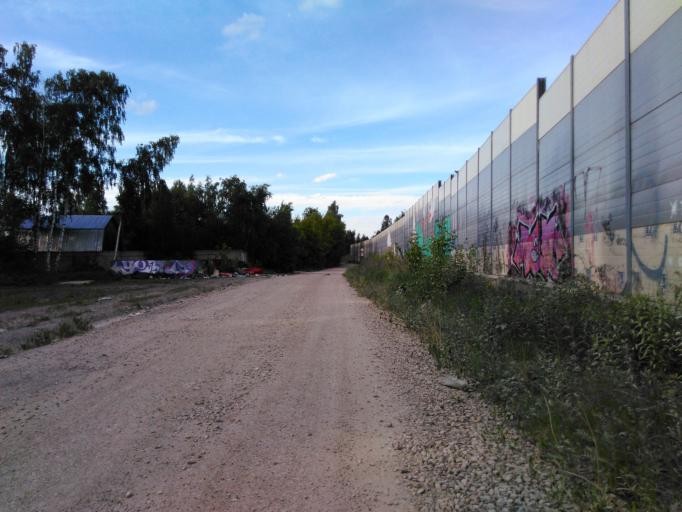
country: RU
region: Moskovskaya
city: Vishnyakovskiye Dachi
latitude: 55.7553
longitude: 38.1393
